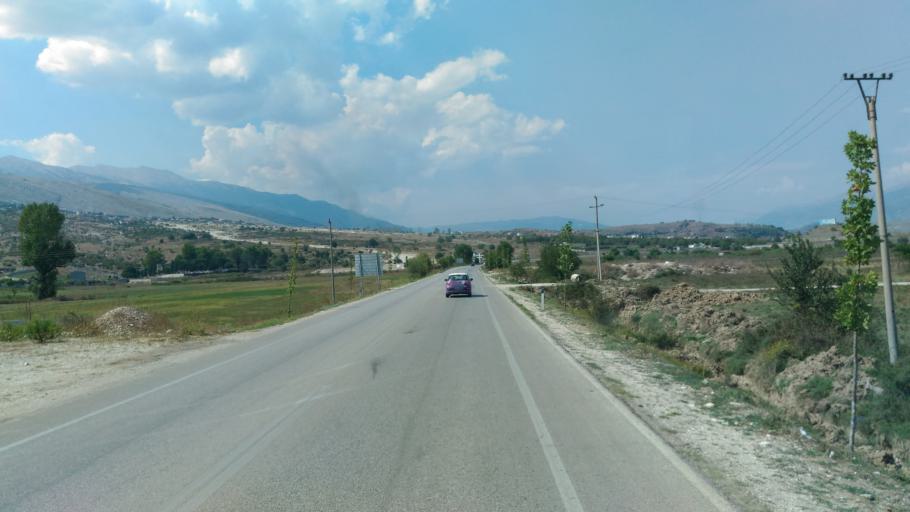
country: AL
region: Gjirokaster
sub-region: Rrethi i Gjirokastres
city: Dervician
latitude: 40.0363
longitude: 20.1796
